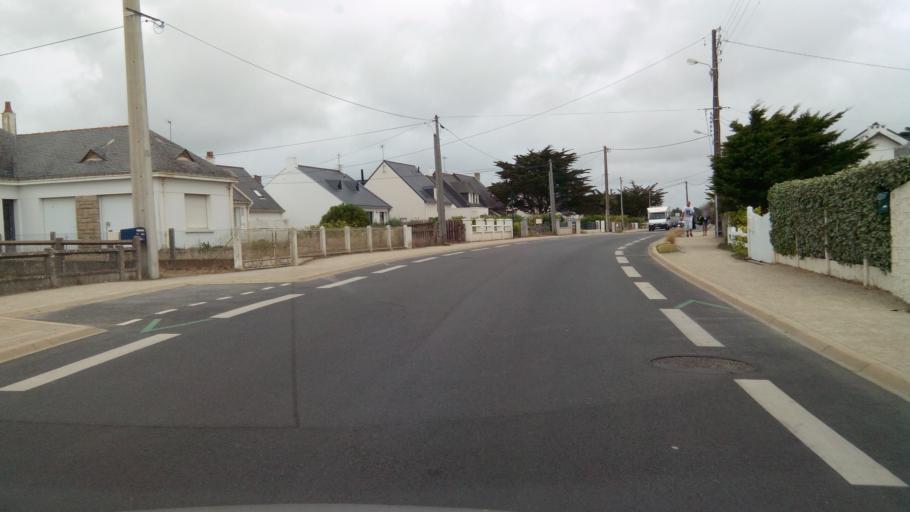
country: FR
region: Pays de la Loire
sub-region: Departement de la Loire-Atlantique
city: Batz-sur-Mer
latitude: 47.2766
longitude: -2.4924
